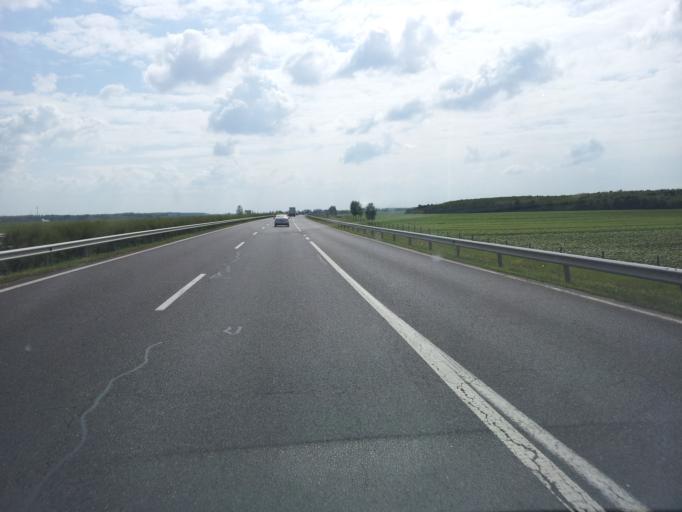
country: HU
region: Borsod-Abauj-Zemplen
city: Emod
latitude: 47.8843
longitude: 20.8743
